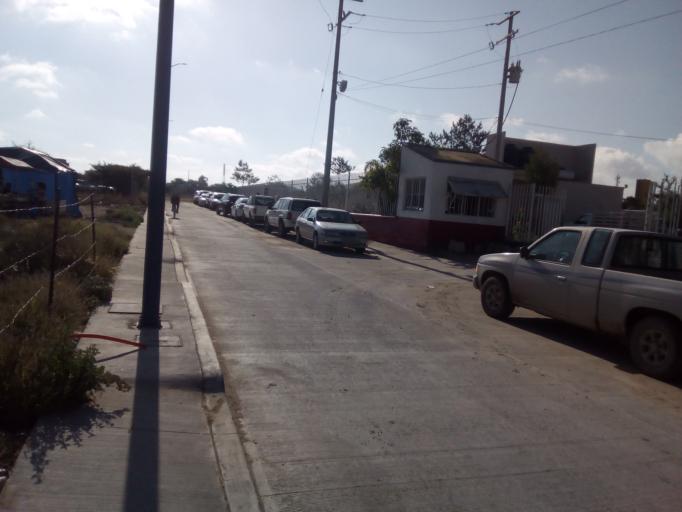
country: MX
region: Guanajuato
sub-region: San Luis de la Paz
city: San Ignacio
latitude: 21.2971
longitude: -100.5326
